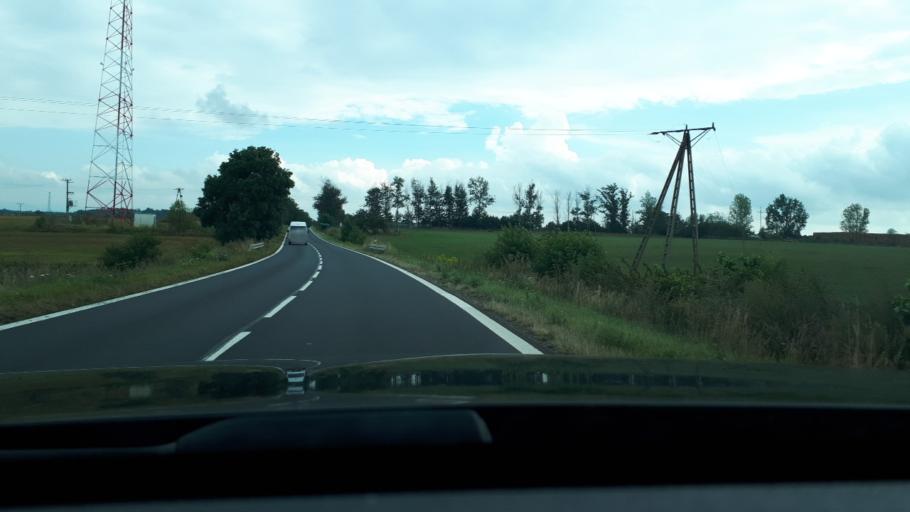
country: PL
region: Lower Silesian Voivodeship
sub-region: Powiat lubanski
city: Pisarzowice
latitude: 51.1760
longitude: 15.2616
